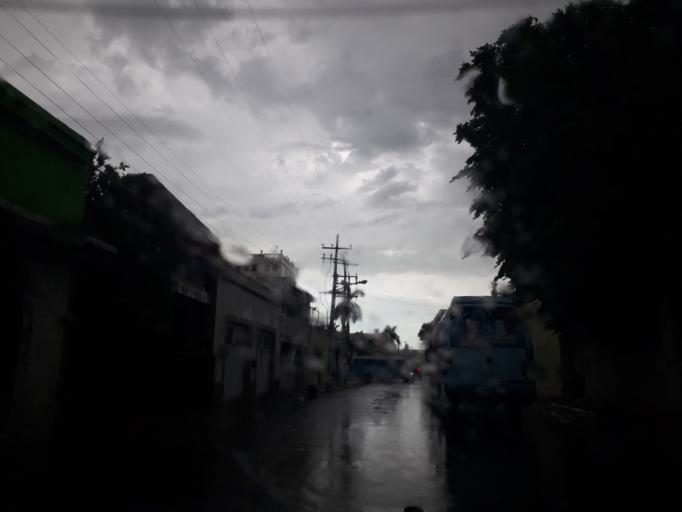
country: MX
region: Yucatan
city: Merida
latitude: 20.9697
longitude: -89.6339
